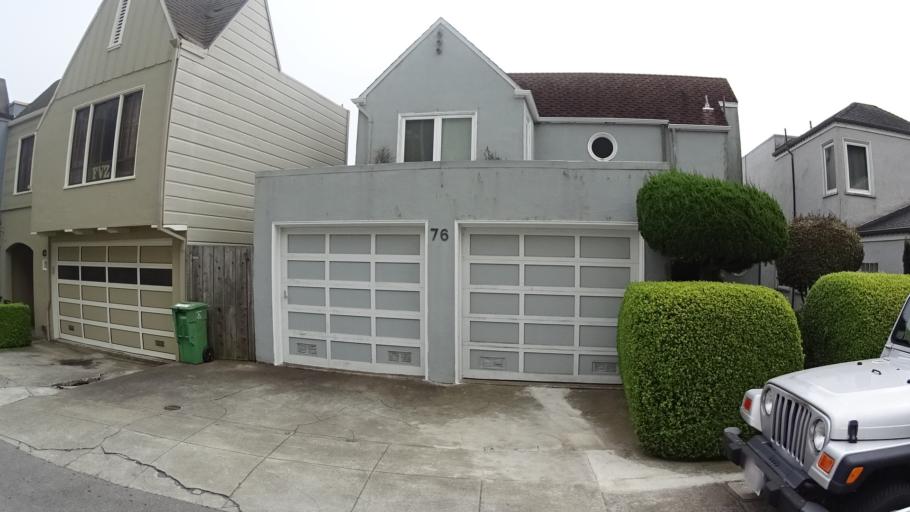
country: US
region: California
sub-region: San Mateo County
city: Daly City
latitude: 37.7348
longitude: -122.4536
